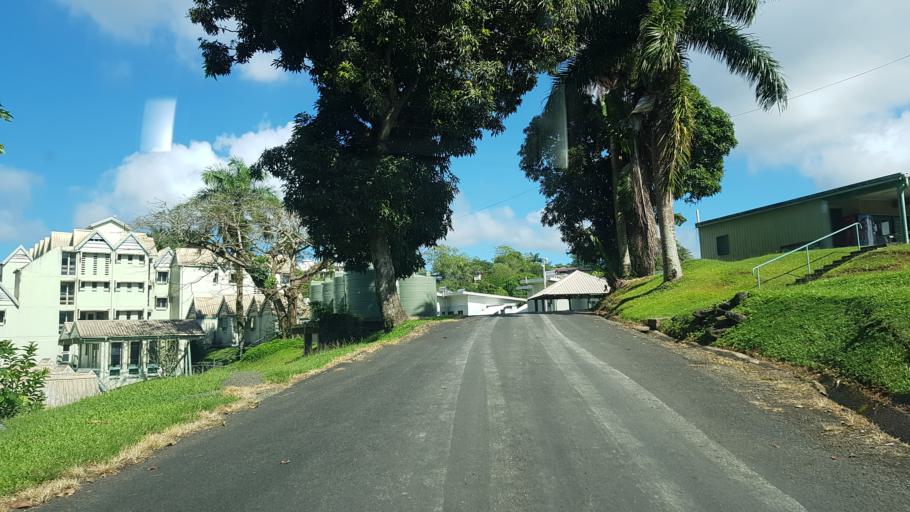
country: FJ
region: Central
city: Suva
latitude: -18.1502
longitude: 178.4417
